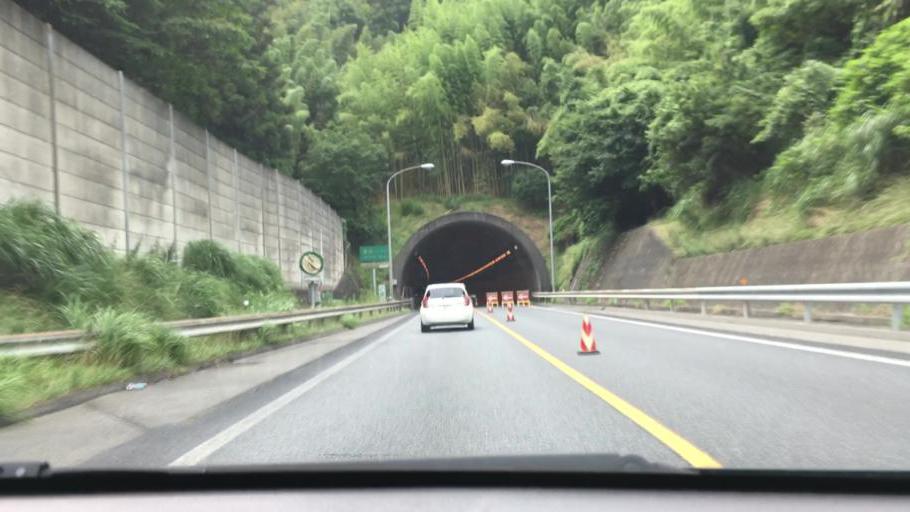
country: JP
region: Yamaguchi
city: Tokuyama
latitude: 34.0888
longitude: 131.7763
